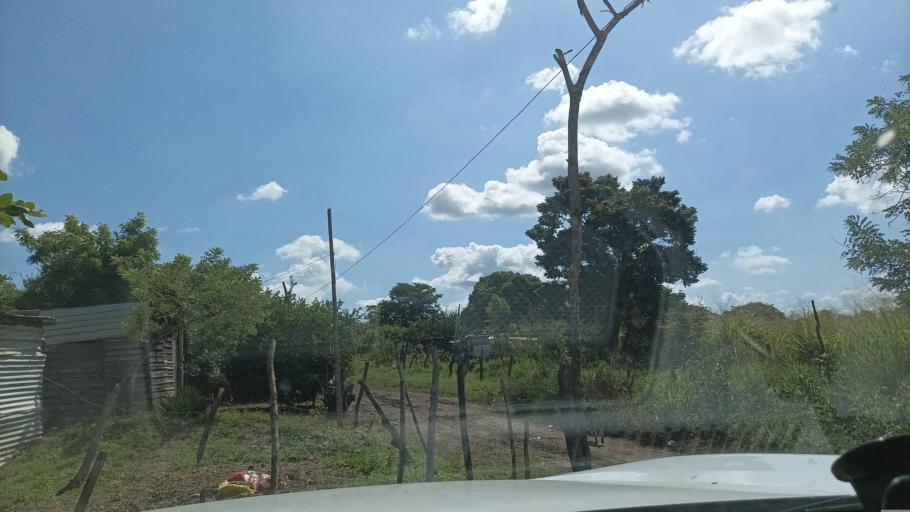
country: MX
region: Veracruz
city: Manlio Fabio Altamirano
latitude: 19.0870
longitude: -96.3441
